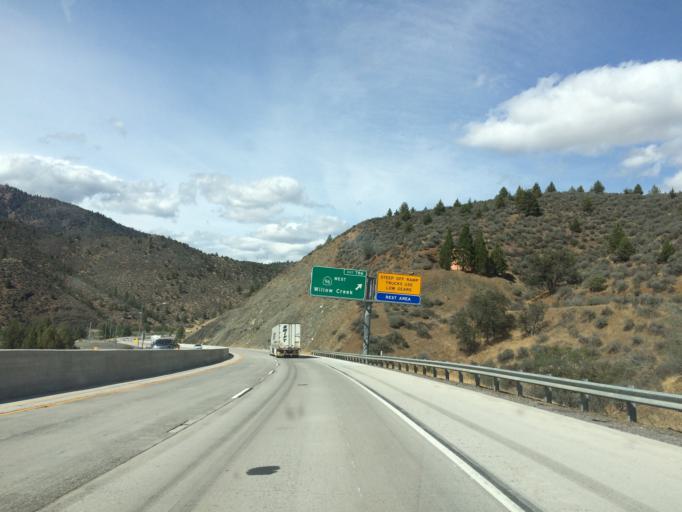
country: US
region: California
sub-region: Siskiyou County
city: Montague
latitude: 41.8491
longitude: -122.5681
